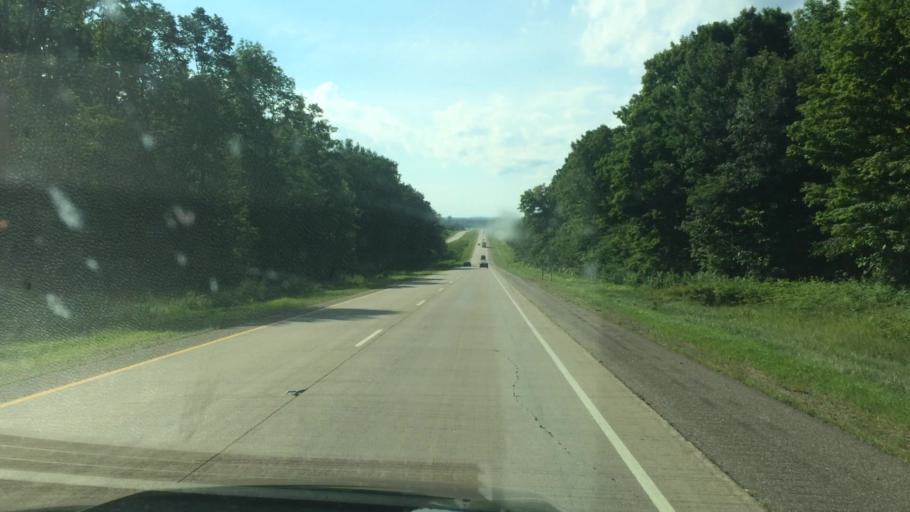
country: US
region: Wisconsin
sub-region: Shawano County
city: Wittenberg
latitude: 44.8181
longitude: -89.0522
